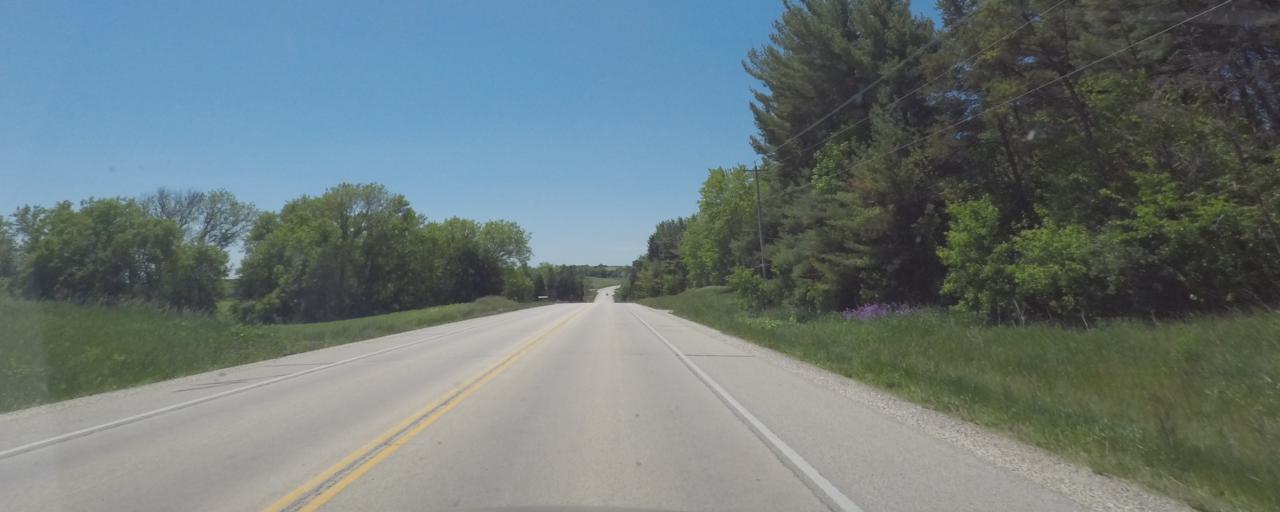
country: US
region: Wisconsin
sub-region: Ozaukee County
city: Kohler
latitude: 43.5336
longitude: -88.0940
